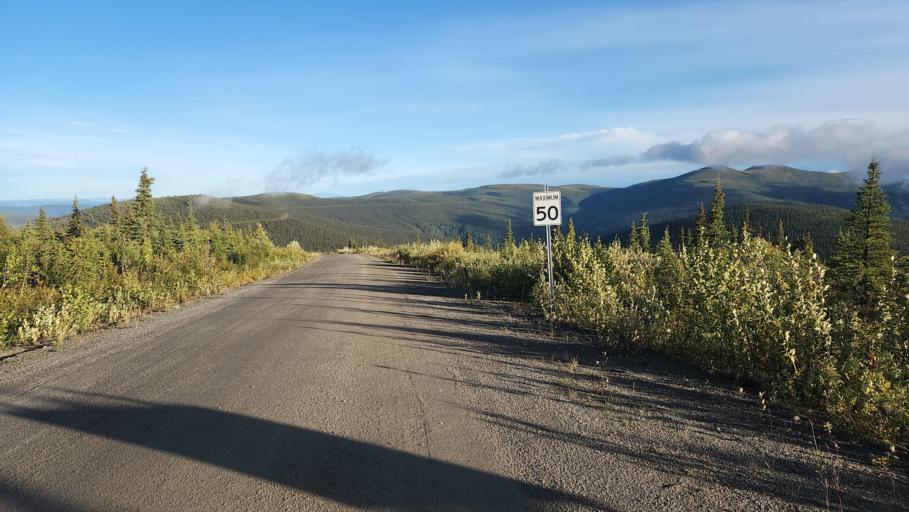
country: CA
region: Yukon
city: Dawson City
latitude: 64.2201
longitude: -140.3160
